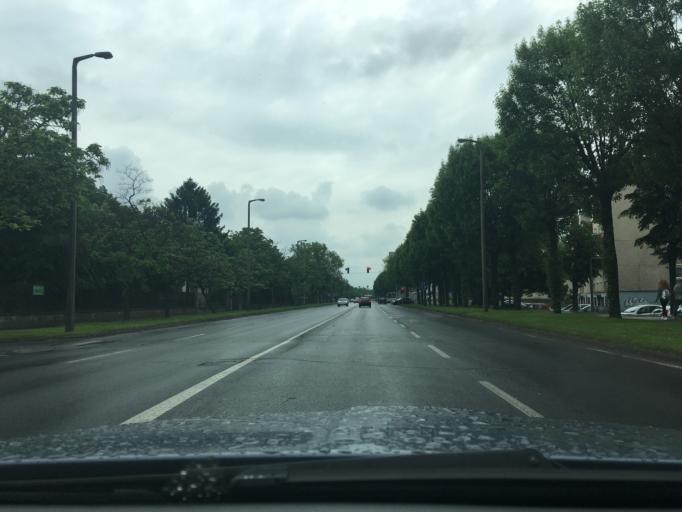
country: HU
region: Hajdu-Bihar
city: Debrecen
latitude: 47.5365
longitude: 21.6117
